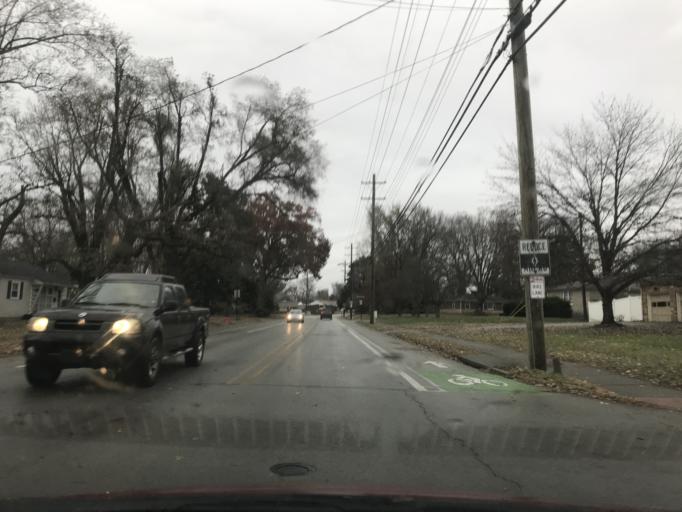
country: US
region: Kentucky
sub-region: Jefferson County
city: West Buechel
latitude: 38.2119
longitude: -85.6625
